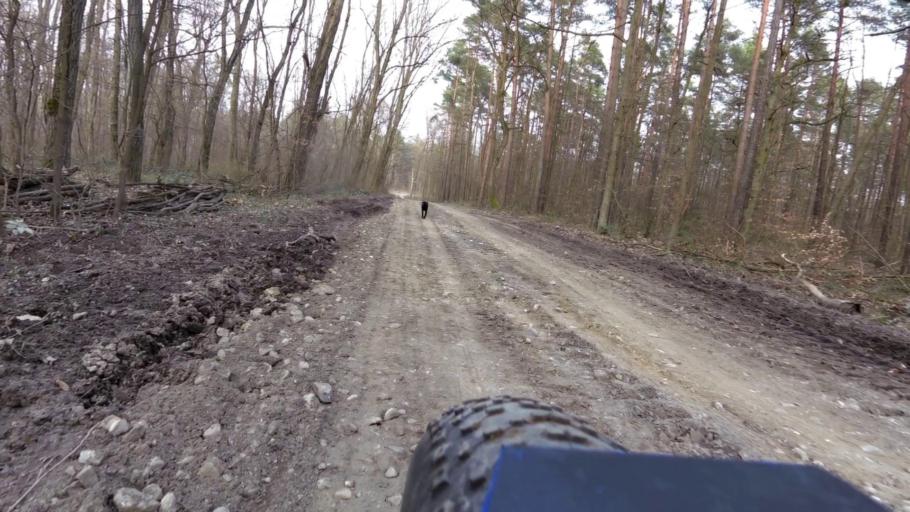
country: DE
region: Brandenburg
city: Vogelsang
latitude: 52.2774
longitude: 14.6994
